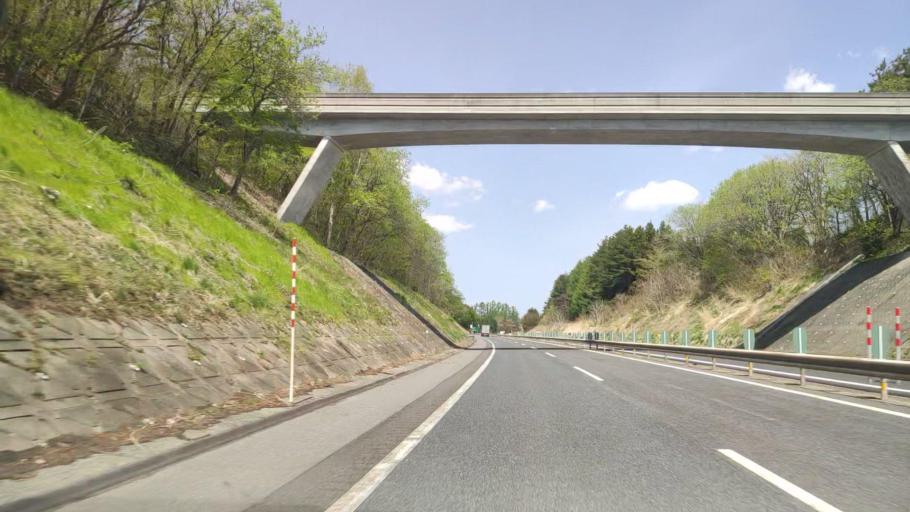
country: JP
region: Aomori
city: Hachinohe
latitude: 40.3974
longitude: 141.4473
